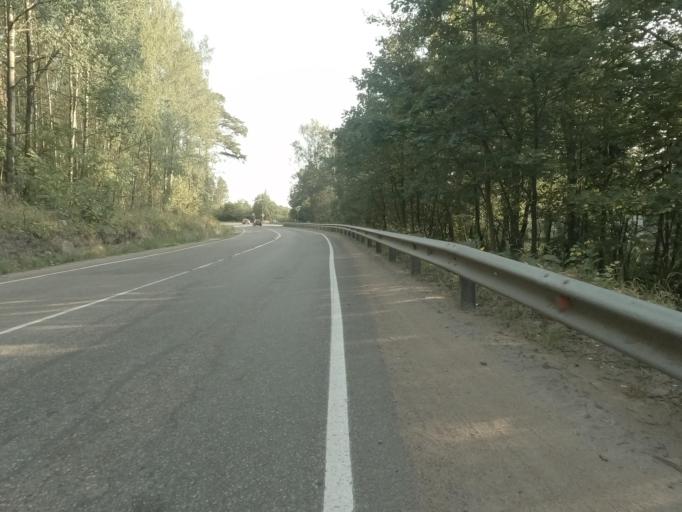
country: RU
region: Leningrad
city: Vyborg
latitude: 60.7376
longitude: 28.7585
